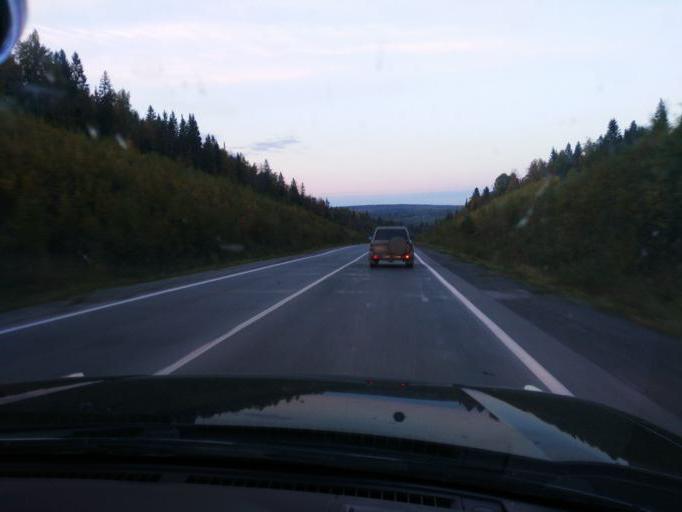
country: RU
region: Perm
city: Sylva
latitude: 58.2927
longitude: 56.7520
